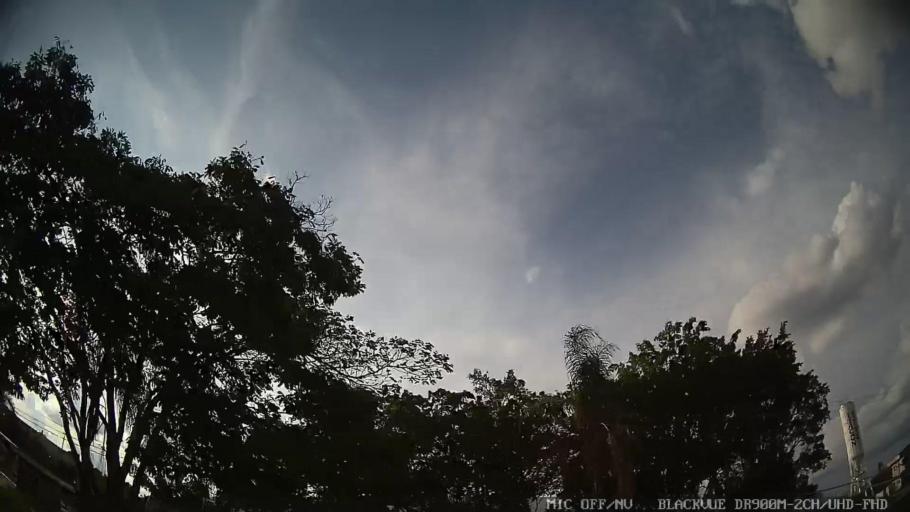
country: BR
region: Sao Paulo
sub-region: Braganca Paulista
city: Braganca Paulista
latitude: -22.9221
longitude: -46.5012
